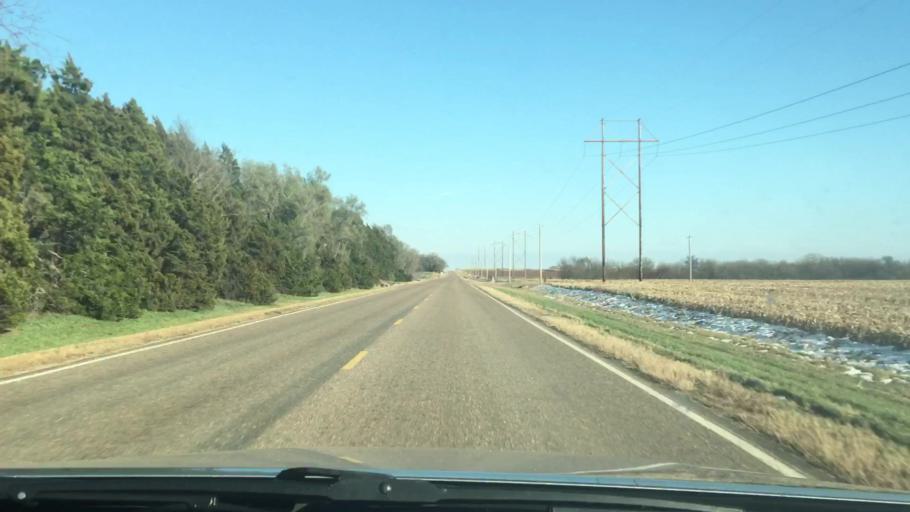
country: US
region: Kansas
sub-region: Rice County
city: Lyons
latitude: 38.2895
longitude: -98.0978
